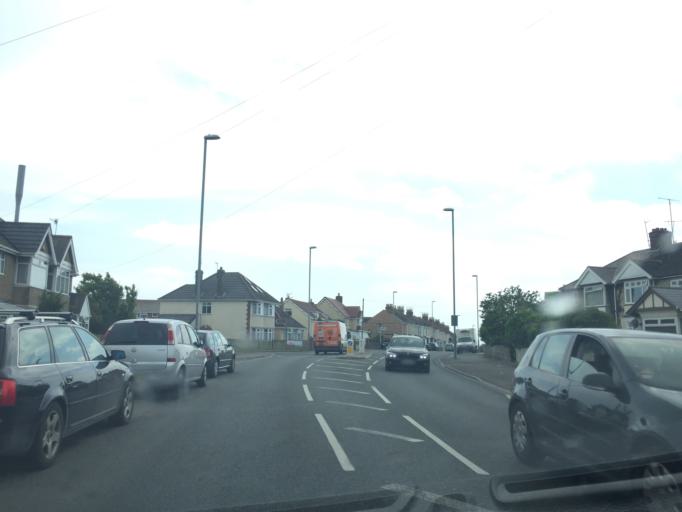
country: GB
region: England
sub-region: Dorset
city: Weymouth
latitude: 50.5888
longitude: -2.4725
